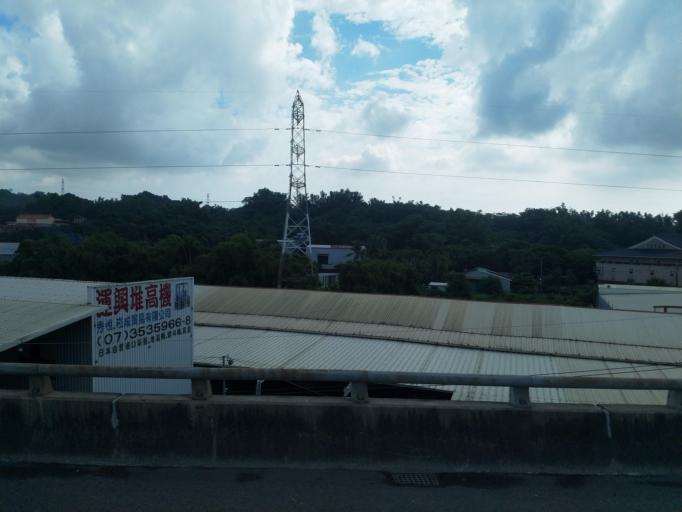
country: TW
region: Taiwan
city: Fengshan
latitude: 22.7172
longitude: 120.3598
